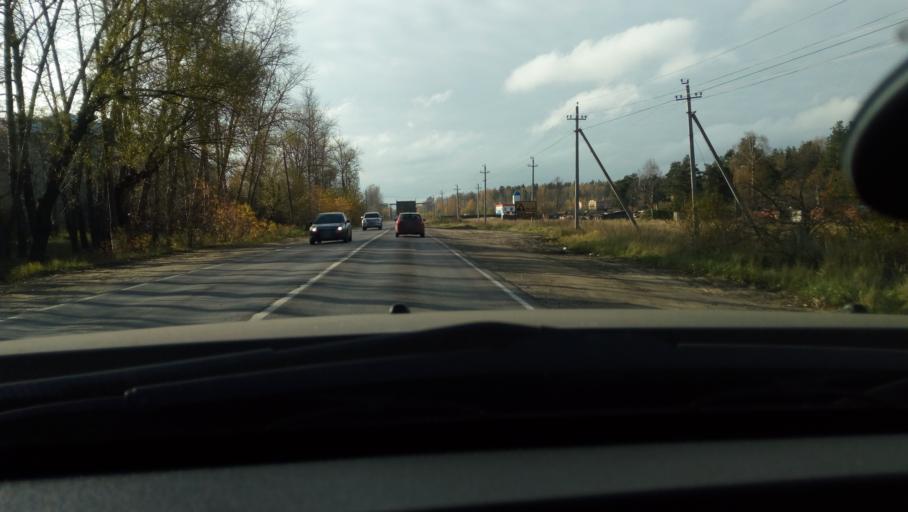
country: RU
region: Moskovskaya
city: Fryazevo
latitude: 55.7151
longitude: 38.4629
